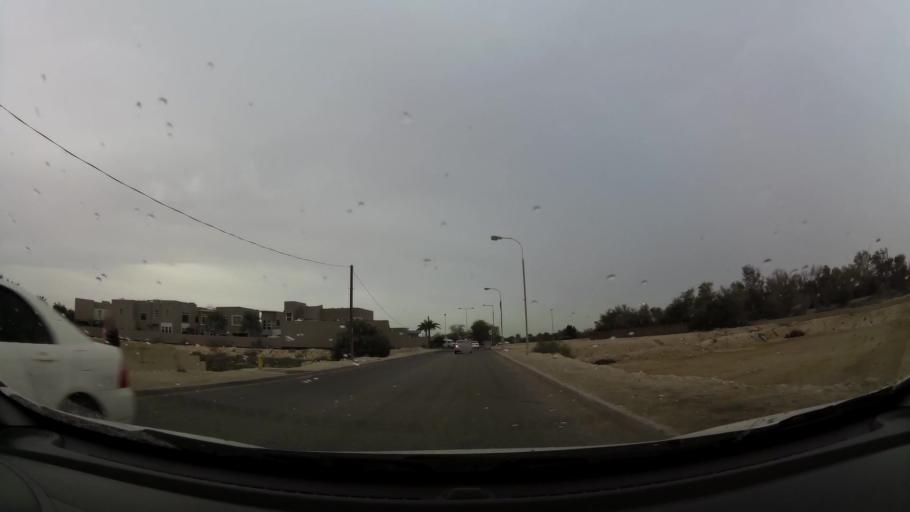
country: BH
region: Central Governorate
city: Madinat Hamad
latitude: 26.1135
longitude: 50.4863
